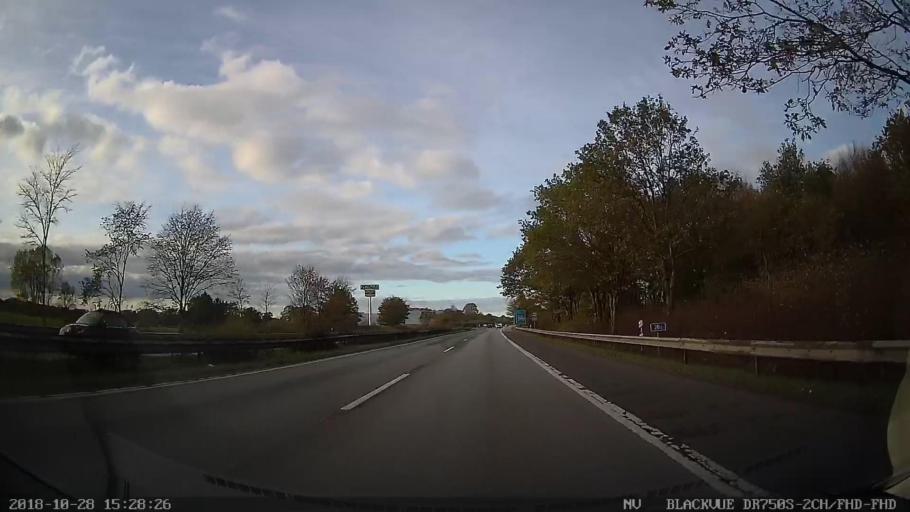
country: DE
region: Schleswig-Holstein
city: Seeth-Ekholt
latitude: 53.7364
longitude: 9.7182
